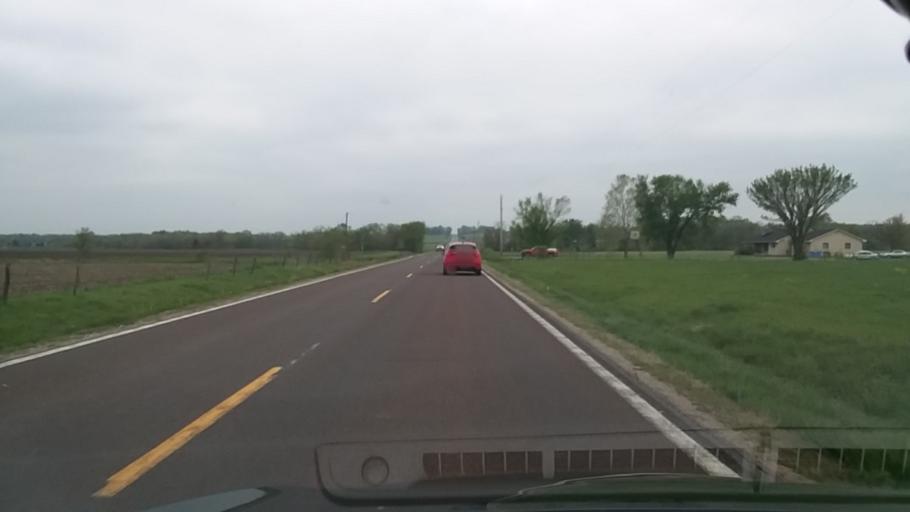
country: US
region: Kansas
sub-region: Douglas County
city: Eudora
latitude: 38.8562
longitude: -95.0933
